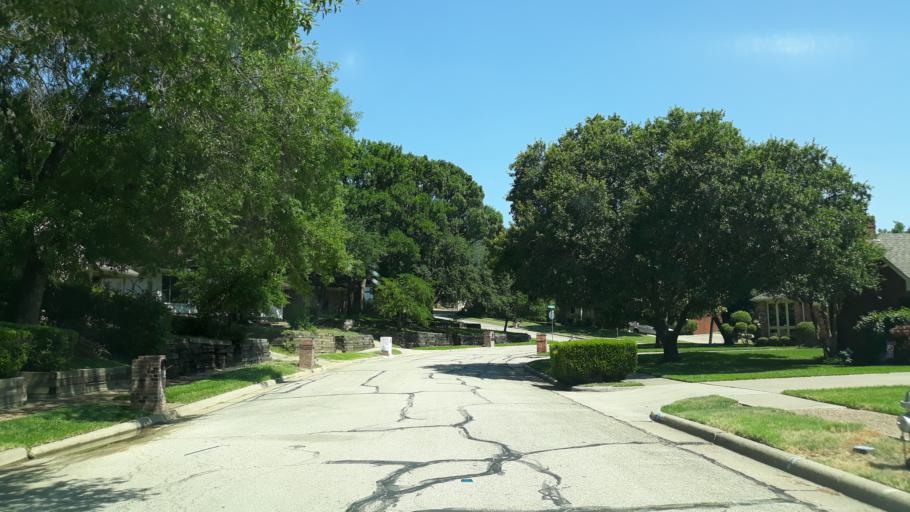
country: US
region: Texas
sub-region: Dallas County
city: Irving
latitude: 32.8239
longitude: -97.0073
